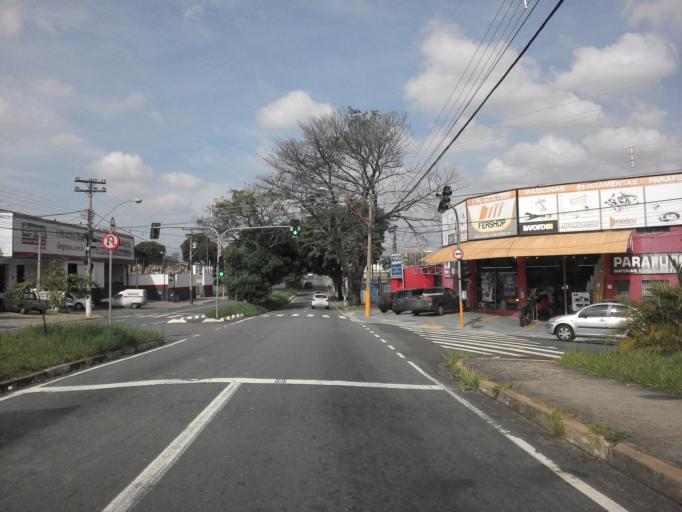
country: BR
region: Sao Paulo
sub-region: Campinas
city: Campinas
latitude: -22.9258
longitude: -47.0487
